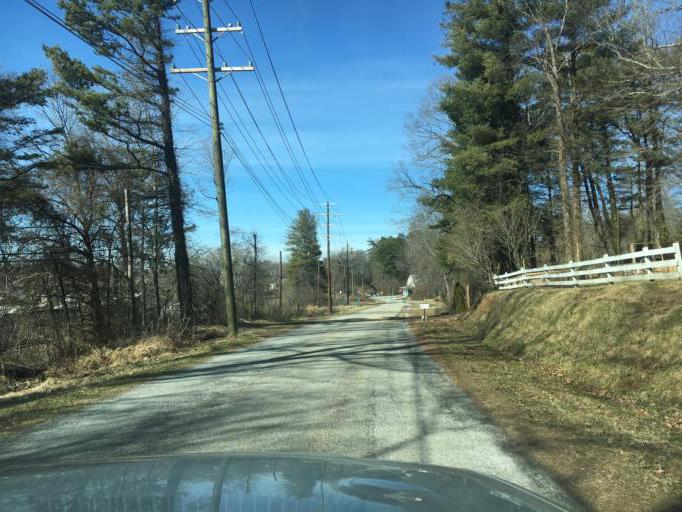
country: US
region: North Carolina
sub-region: Henderson County
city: Mountain Home
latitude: 35.3915
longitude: -82.5000
